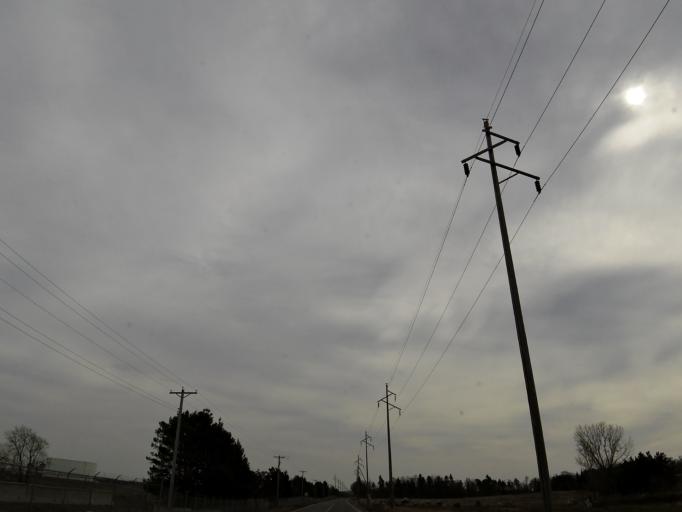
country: US
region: Minnesota
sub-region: Dakota County
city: Rosemount
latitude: 44.7727
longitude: -93.0593
